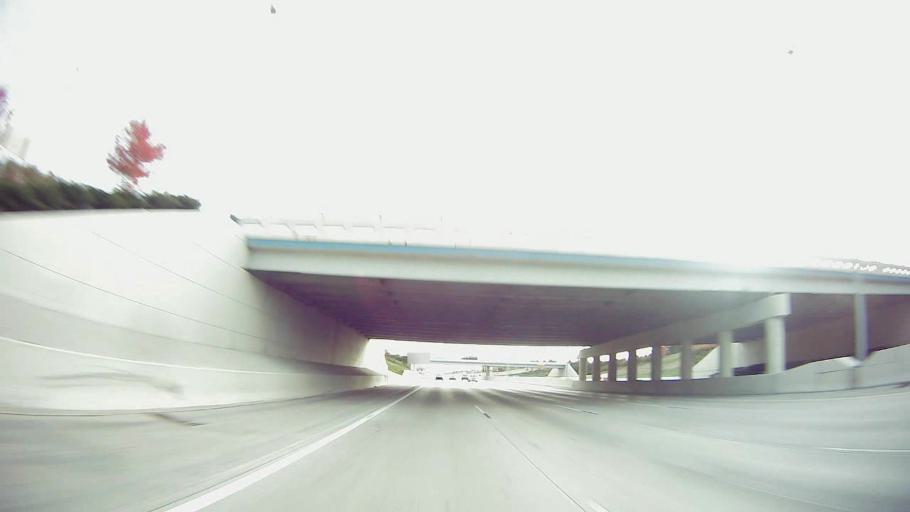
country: US
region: Michigan
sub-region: Wayne County
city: Livonia
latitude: 42.3836
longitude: -83.3341
